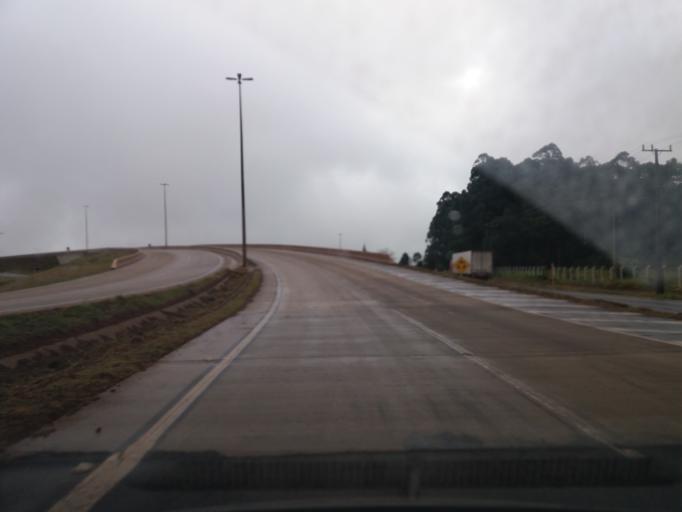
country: BR
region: Parana
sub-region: Cascavel
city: Cascavel
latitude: -25.1493
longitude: -53.5928
